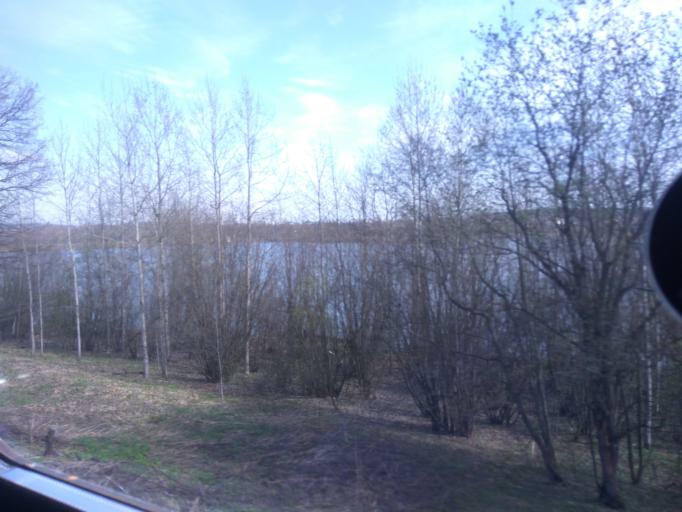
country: RU
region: Moskovskaya
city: Yermolino
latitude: 56.1496
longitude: 37.5053
